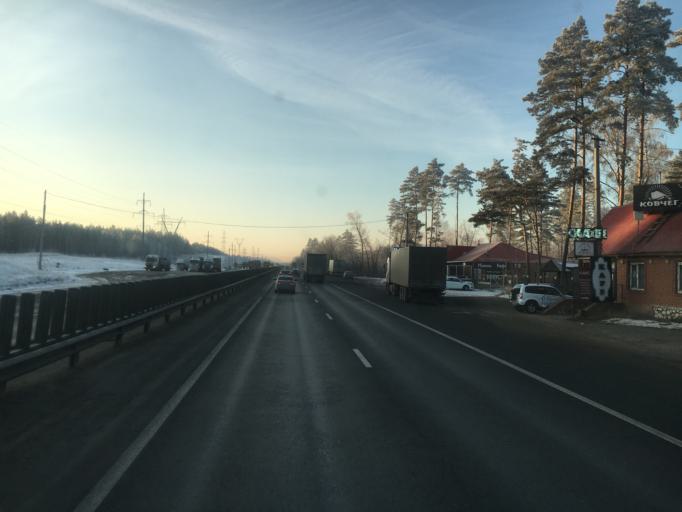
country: RU
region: Samara
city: Pribrezhnyy
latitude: 53.5138
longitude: 49.9036
